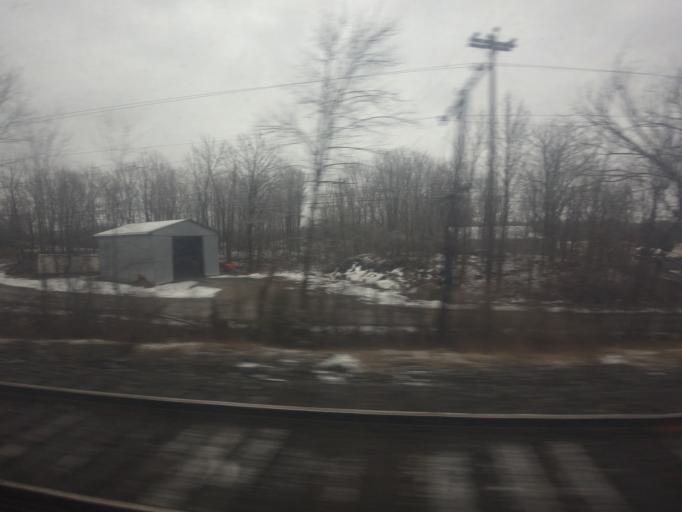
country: CA
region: Ontario
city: Gananoque
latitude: 44.3598
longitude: -76.1877
